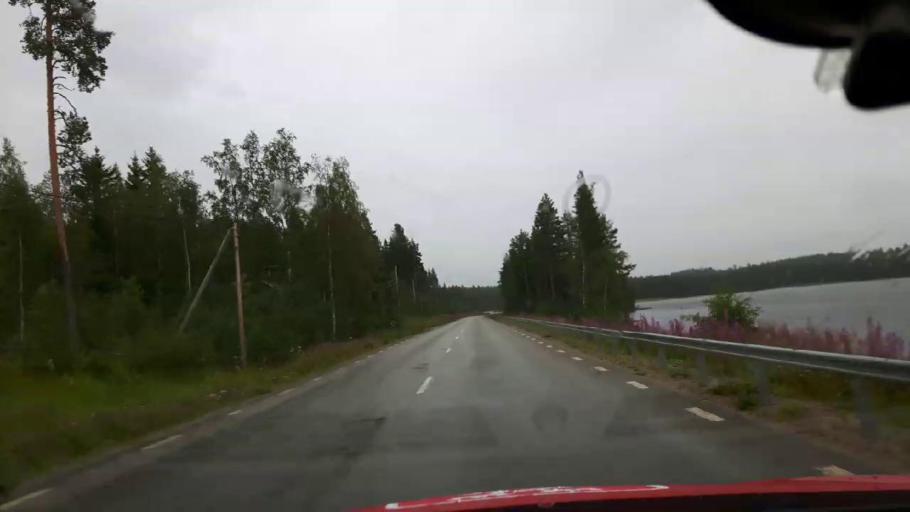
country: SE
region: Jaemtland
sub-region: OEstersunds Kommun
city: Brunflo
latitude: 62.7823
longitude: 15.0111
